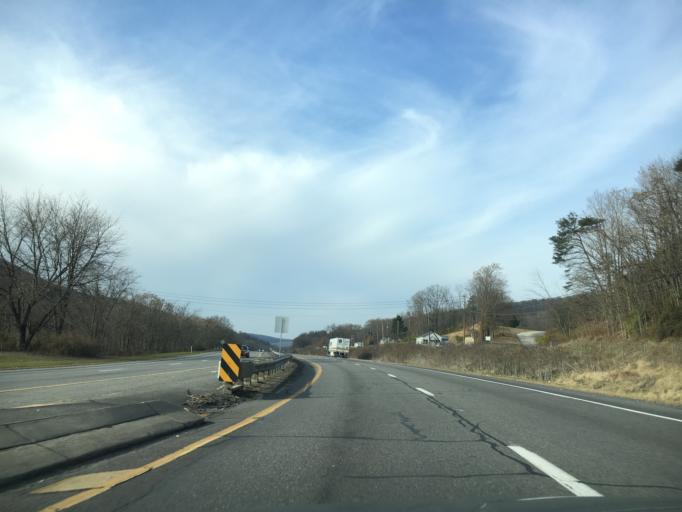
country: US
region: Pennsylvania
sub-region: Montour County
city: Danville
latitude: 40.9724
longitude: -76.6171
